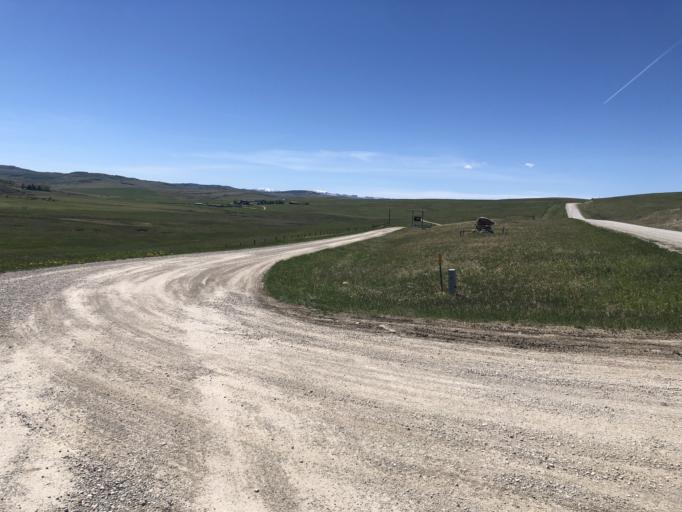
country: CA
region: Alberta
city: Nanton
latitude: 50.3430
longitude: -114.0947
